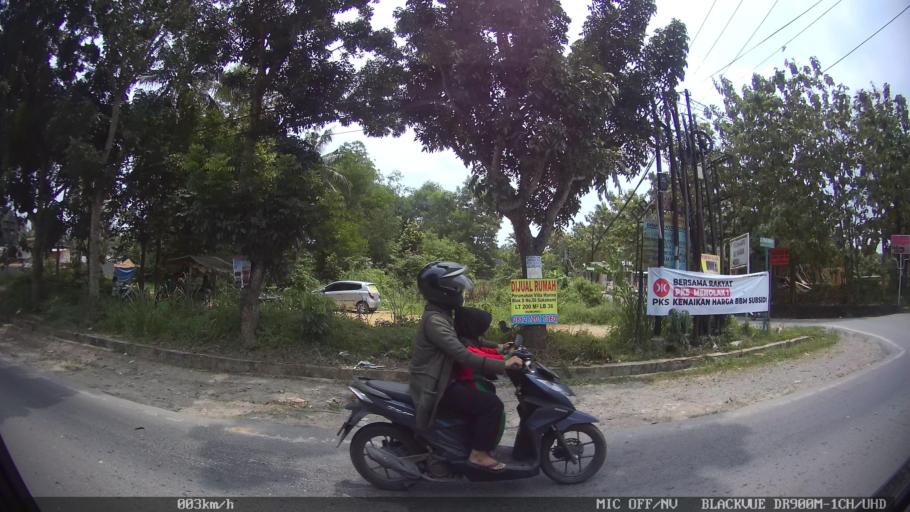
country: ID
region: Lampung
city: Kedaton
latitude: -5.4027
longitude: 105.3158
